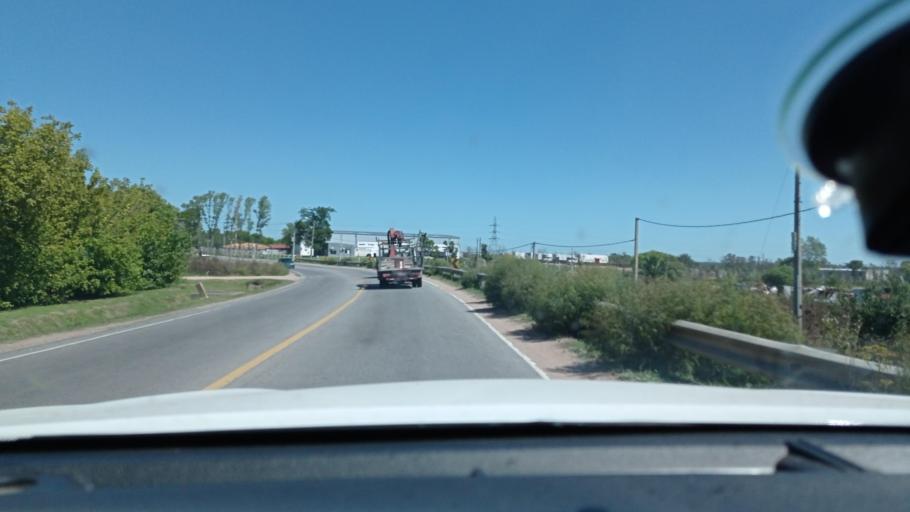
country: UY
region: Canelones
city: La Paz
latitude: -34.7829
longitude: -56.1679
